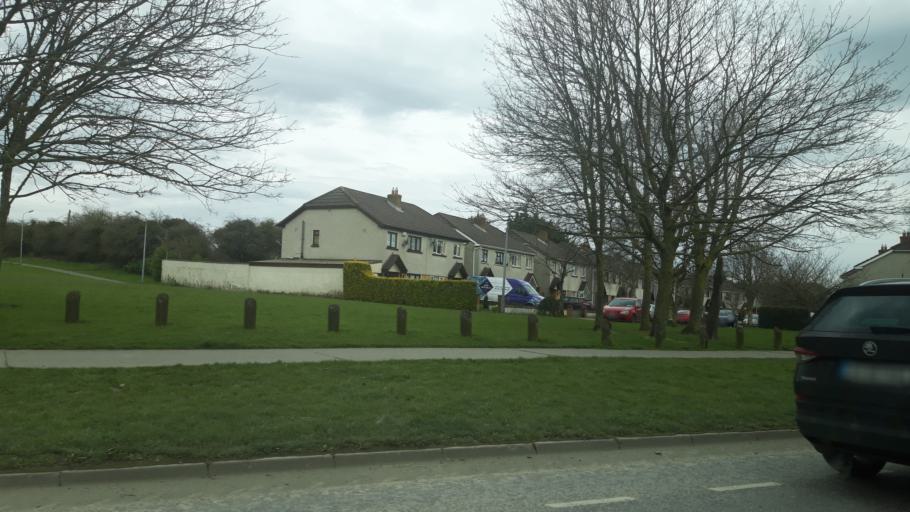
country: IE
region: Leinster
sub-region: Kildare
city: Clane
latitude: 53.2939
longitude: -6.6911
